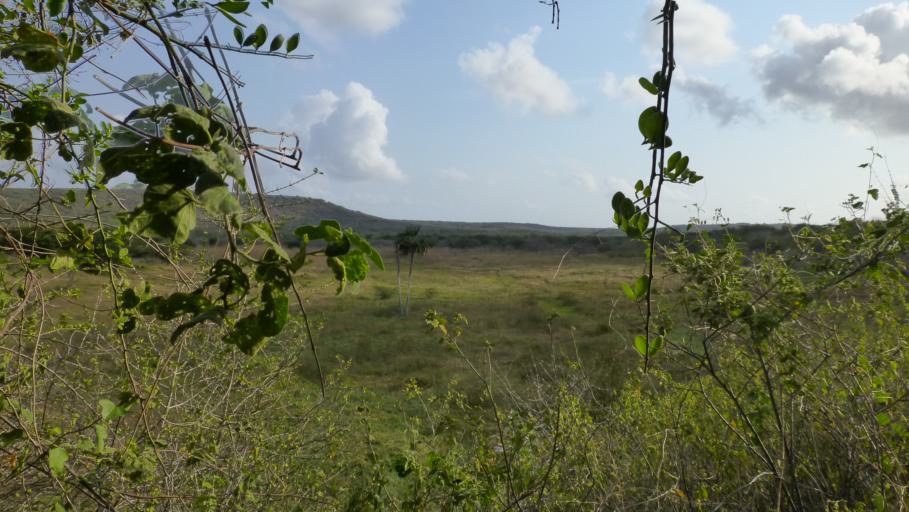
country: CW
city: Sint Michiel Liber
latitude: 12.1684
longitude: -68.9985
